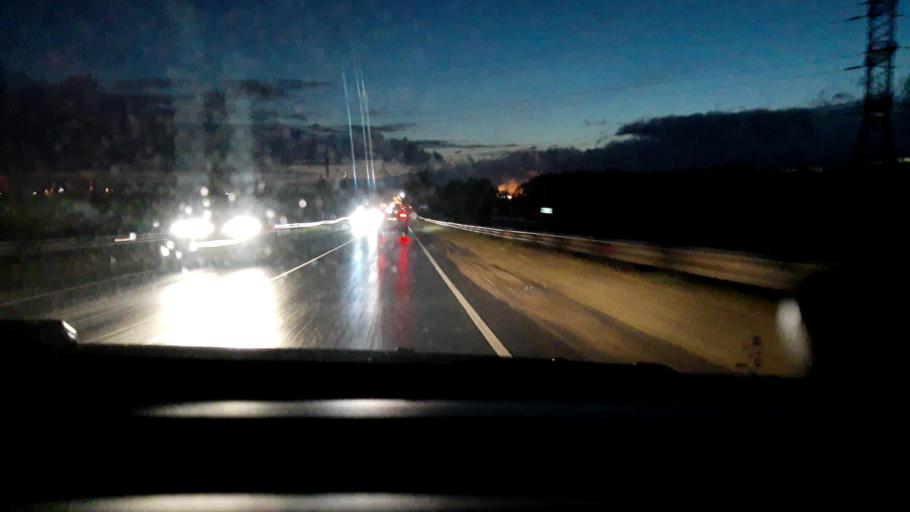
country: RU
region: Nizjnij Novgorod
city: Kstovo
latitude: 56.1290
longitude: 44.1728
